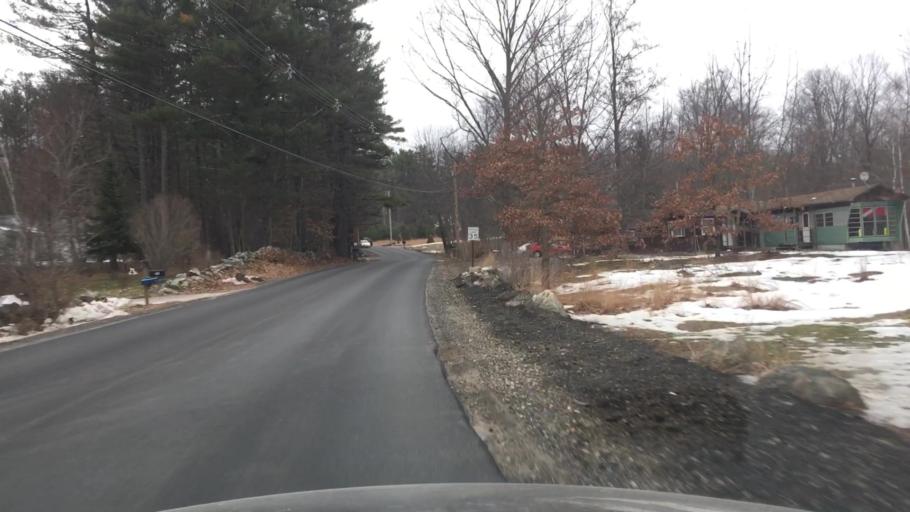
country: US
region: New Hampshire
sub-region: Hillsborough County
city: Goffstown
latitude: 42.9657
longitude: -71.6199
